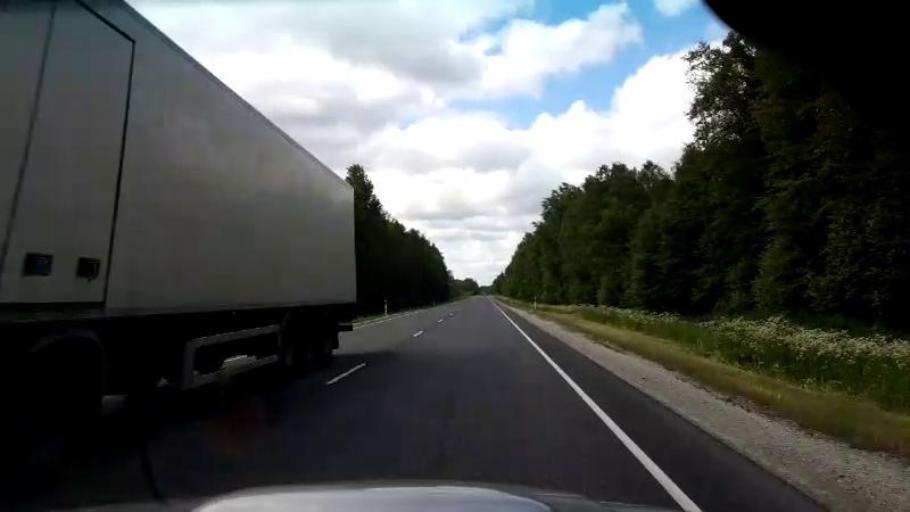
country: EE
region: Raplamaa
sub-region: Maerjamaa vald
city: Marjamaa
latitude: 58.8375
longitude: 24.4221
